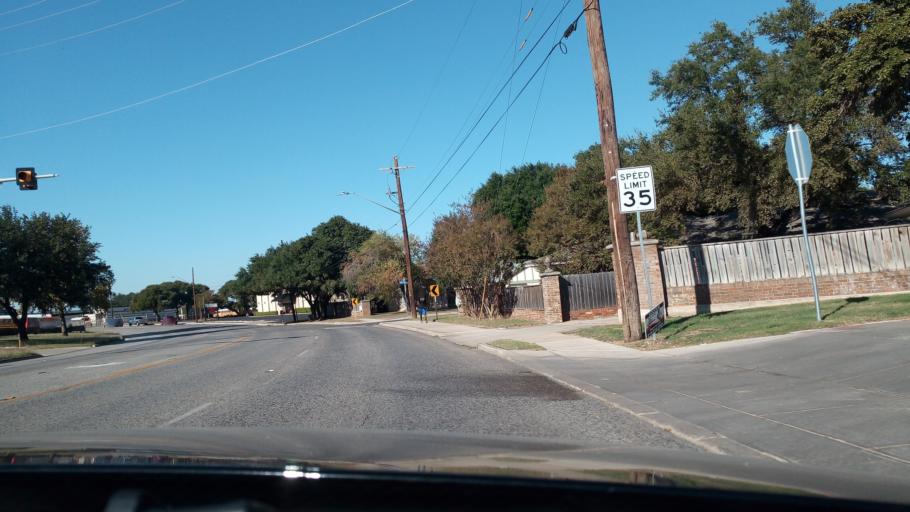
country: US
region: Texas
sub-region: Bexar County
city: Alamo Heights
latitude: 29.5340
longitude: -98.4473
